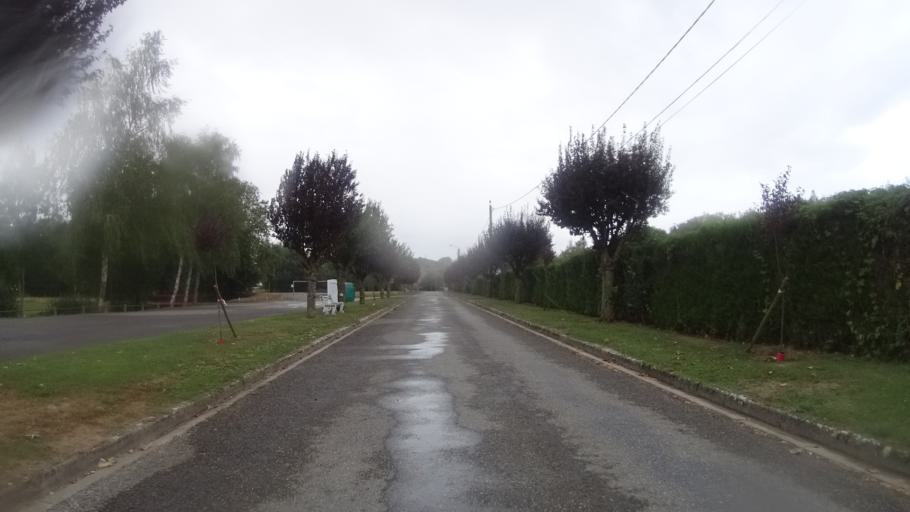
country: FR
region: Picardie
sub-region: Departement de l'Aisne
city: Ribemont
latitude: 49.8267
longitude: 3.4681
